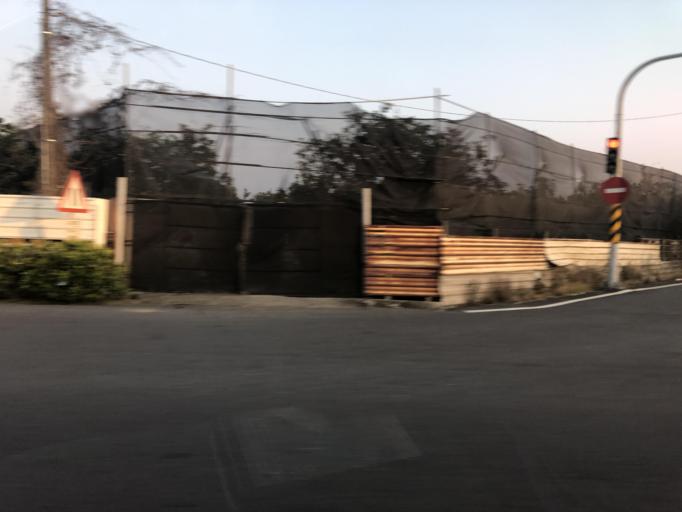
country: TW
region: Taiwan
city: Xinying
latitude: 23.1990
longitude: 120.2666
